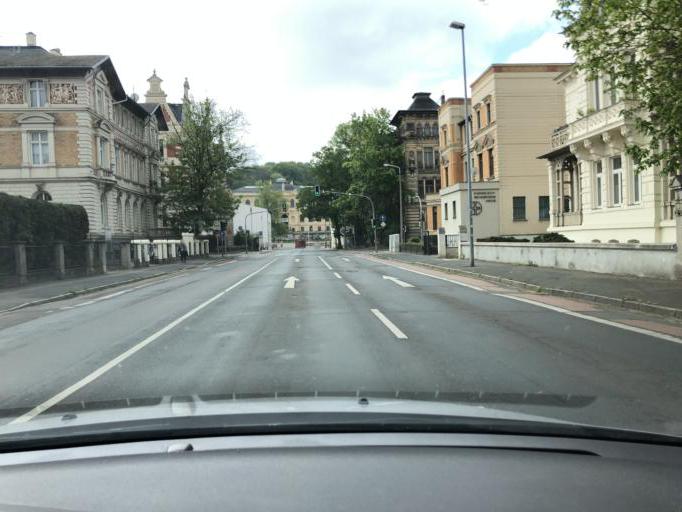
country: DE
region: Thuringia
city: Altenburg
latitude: 50.9939
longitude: 12.4439
